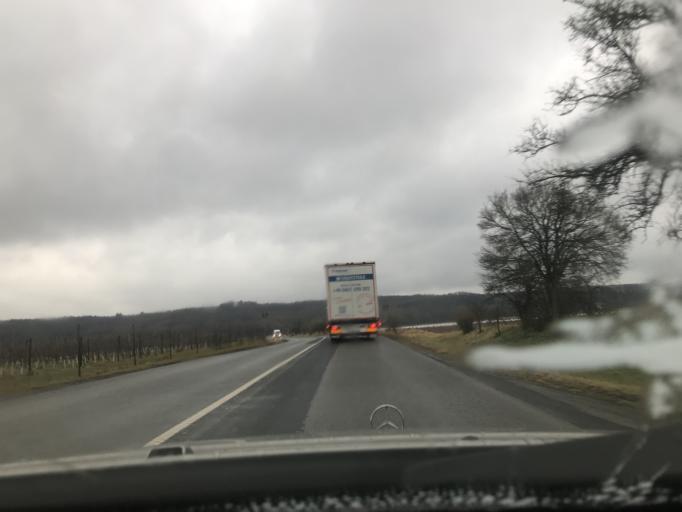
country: DE
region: Hesse
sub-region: Regierungsbezirk Kassel
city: Calden
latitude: 51.4058
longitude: 9.4161
